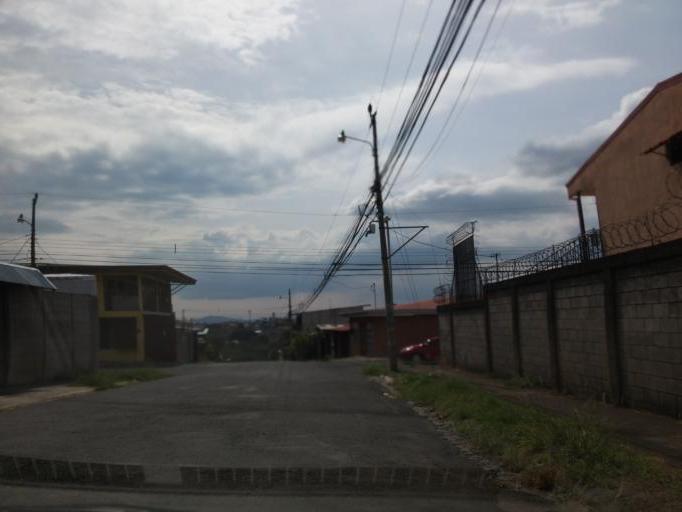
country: CR
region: Alajuela
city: Alajuela
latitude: 10.0122
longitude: -84.1971
